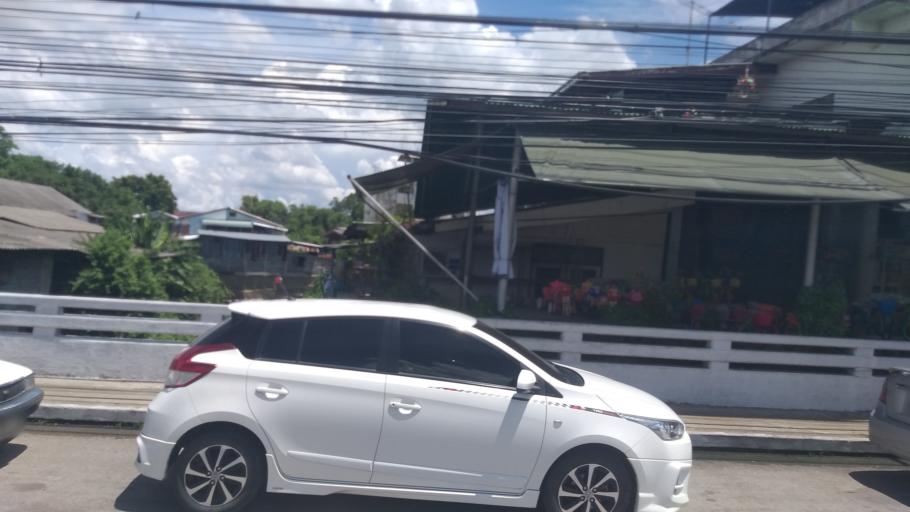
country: TH
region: Nakhon Nayok
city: Ban Na
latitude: 14.2617
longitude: 101.0688
